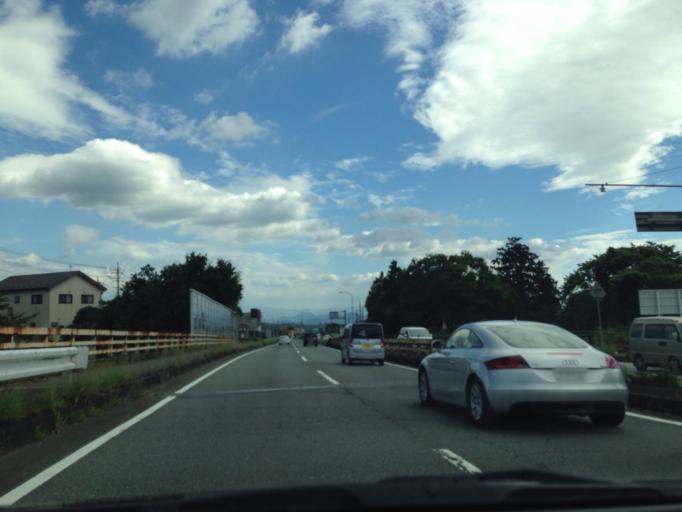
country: JP
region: Shizuoka
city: Gotemba
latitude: 35.2134
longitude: 138.9174
